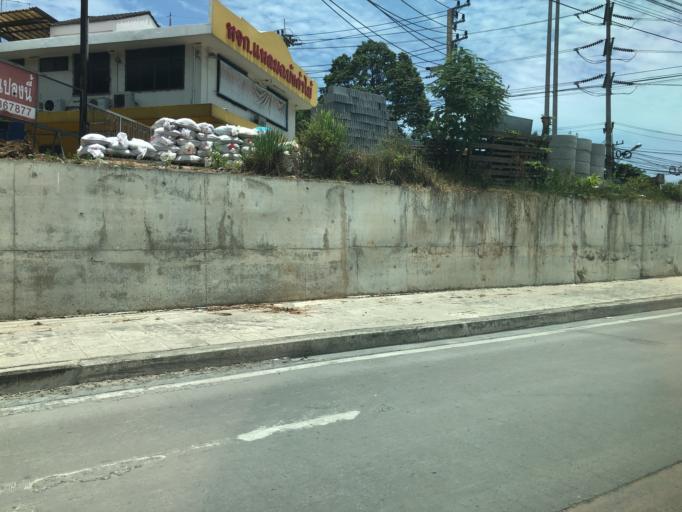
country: TH
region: Chon Buri
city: Bang Lamung
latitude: 13.1102
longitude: 100.9338
